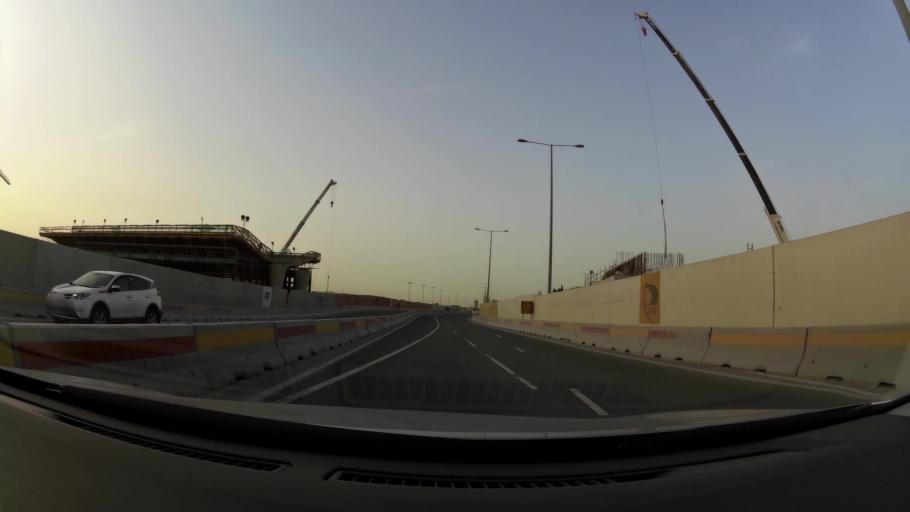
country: QA
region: Baladiyat ad Dawhah
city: Doha
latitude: 25.3519
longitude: 51.5209
